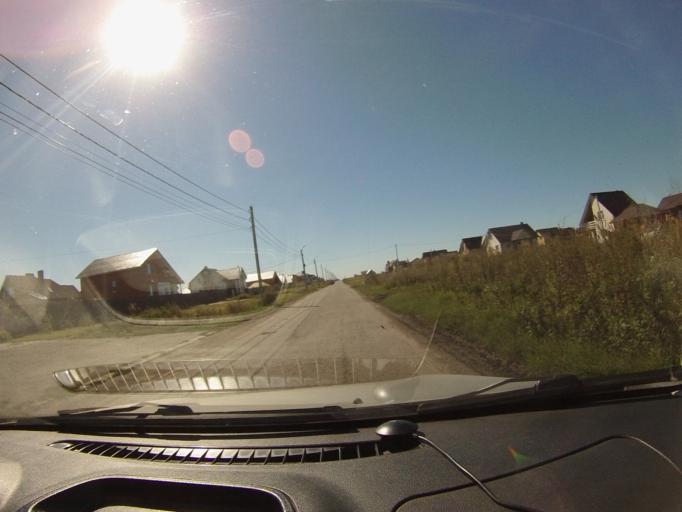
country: RU
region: Tambov
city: Komsomolets
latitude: 52.7759
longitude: 41.3672
